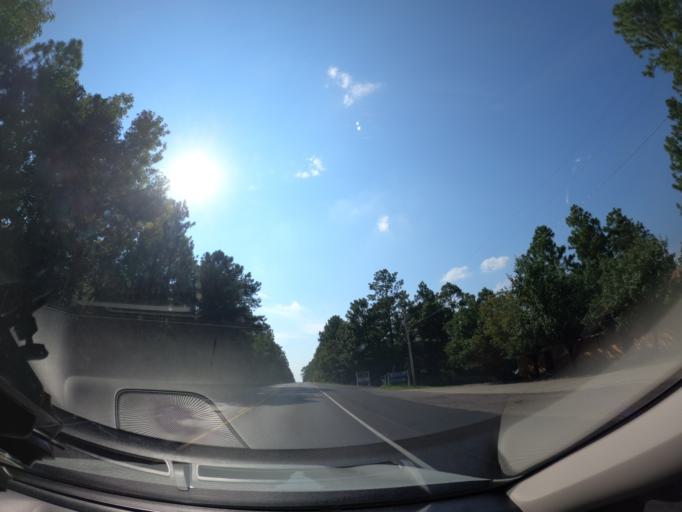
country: US
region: South Carolina
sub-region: Aiken County
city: Jackson
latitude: 33.4029
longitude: -81.7702
